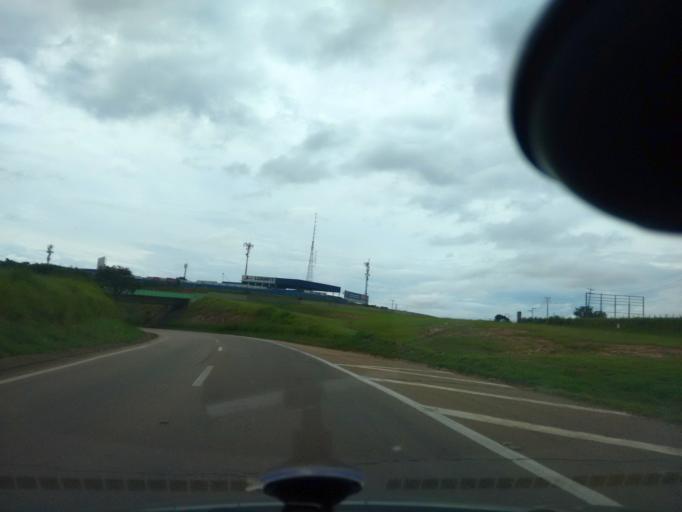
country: BR
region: Sao Paulo
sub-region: Campinas
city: Campinas
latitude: -22.9916
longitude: -47.1081
